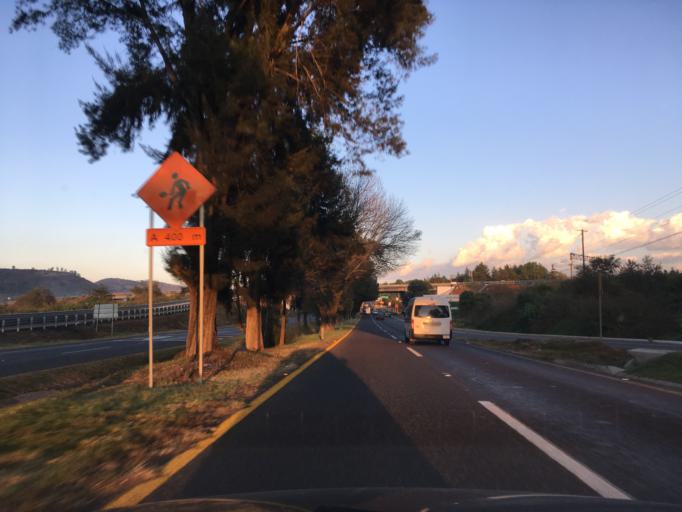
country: MX
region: Michoacan
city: Patzcuaro
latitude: 19.5310
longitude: -101.5586
